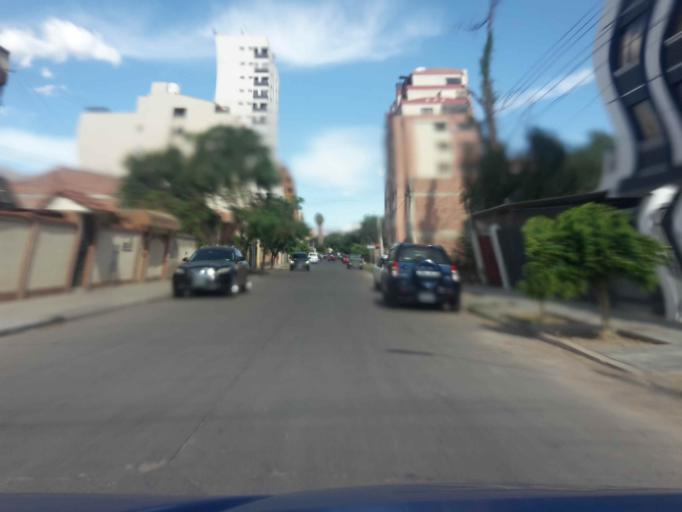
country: BO
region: Cochabamba
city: Cochabamba
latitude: -17.3777
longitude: -66.1779
